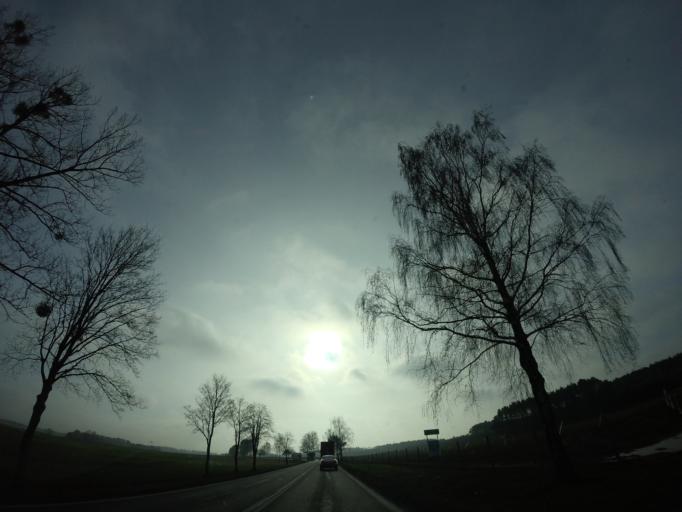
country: PL
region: West Pomeranian Voivodeship
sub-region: Powiat walecki
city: Walcz
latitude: 53.3217
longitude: 16.3154
